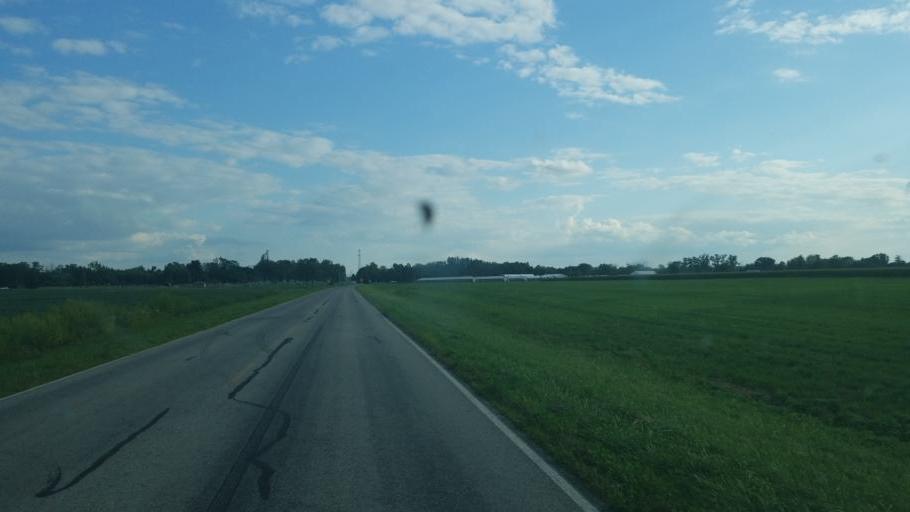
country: US
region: Ohio
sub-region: Seneca County
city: Tiffin
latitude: 41.1261
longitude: -83.1498
